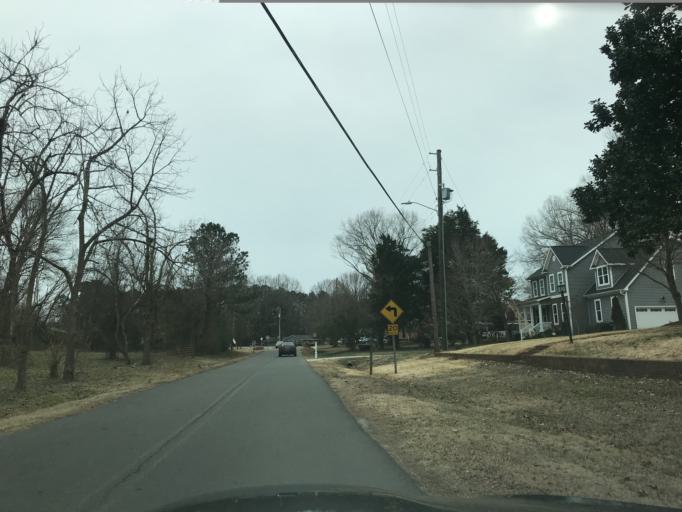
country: US
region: North Carolina
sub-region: Wake County
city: Raleigh
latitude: 35.8668
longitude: -78.6000
